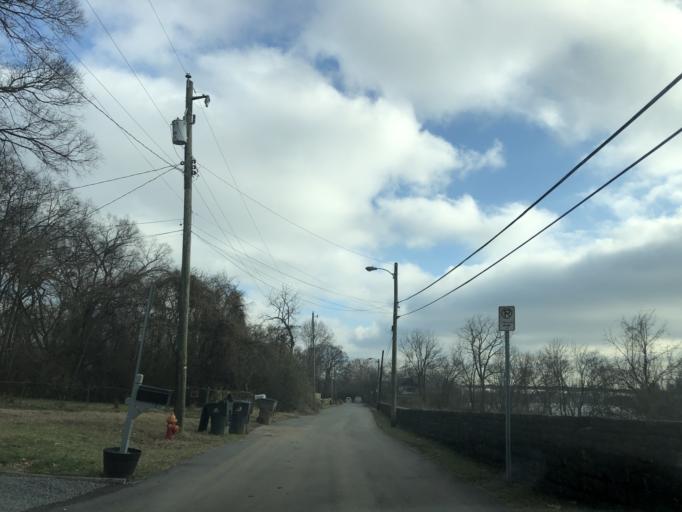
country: US
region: Tennessee
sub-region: Davidson County
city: Nashville
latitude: 36.1990
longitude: -86.7864
